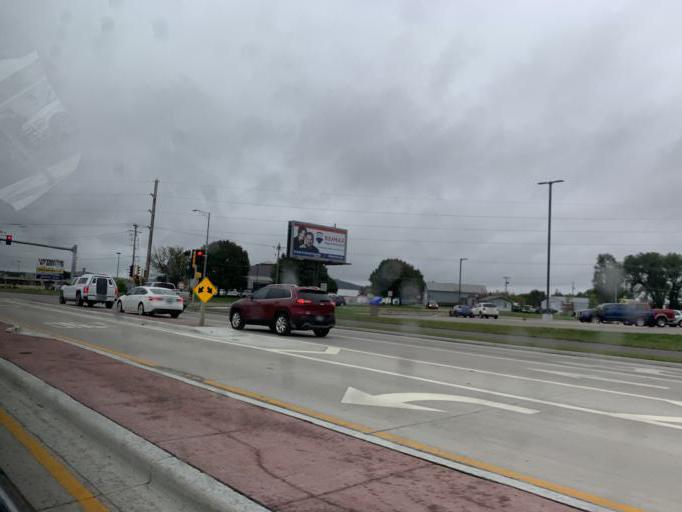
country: US
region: Wisconsin
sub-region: Crawford County
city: Prairie du Chien
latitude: 43.0290
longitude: -91.1286
